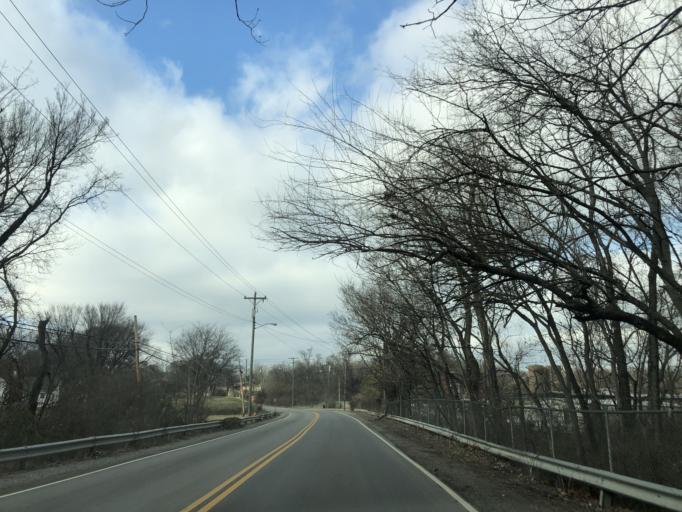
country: US
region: Tennessee
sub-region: Davidson County
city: Nashville
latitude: 36.1982
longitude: -86.7841
